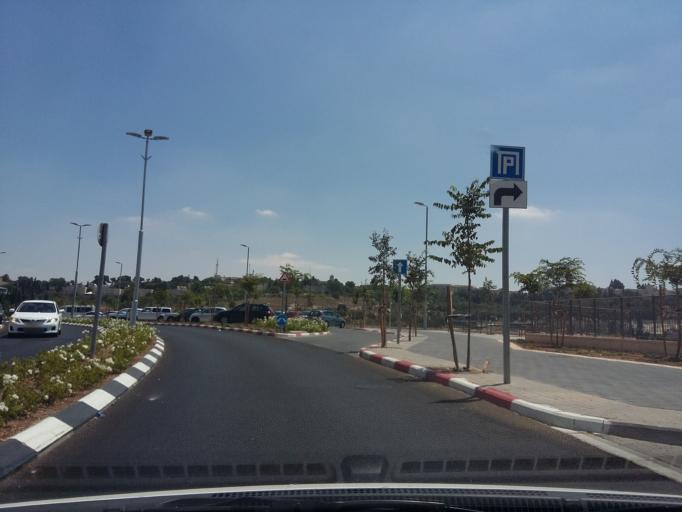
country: PS
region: West Bank
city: East Jerusalem
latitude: 31.7930
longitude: 35.2339
